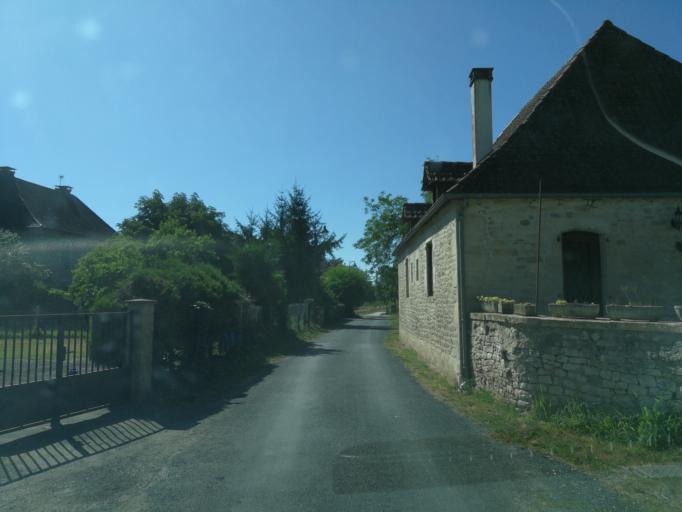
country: FR
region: Midi-Pyrenees
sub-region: Departement du Lot
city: Souillac
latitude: 44.8695
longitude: 1.4359
